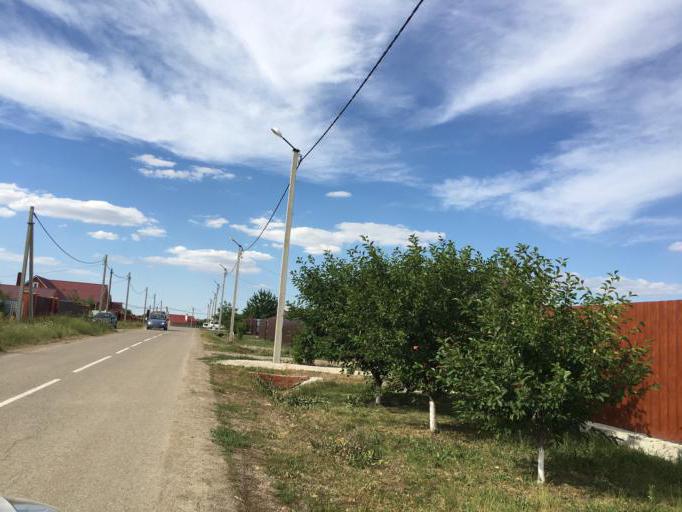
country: RU
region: Krasnodarskiy
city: Kushchevskaya
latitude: 46.5517
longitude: 39.6739
